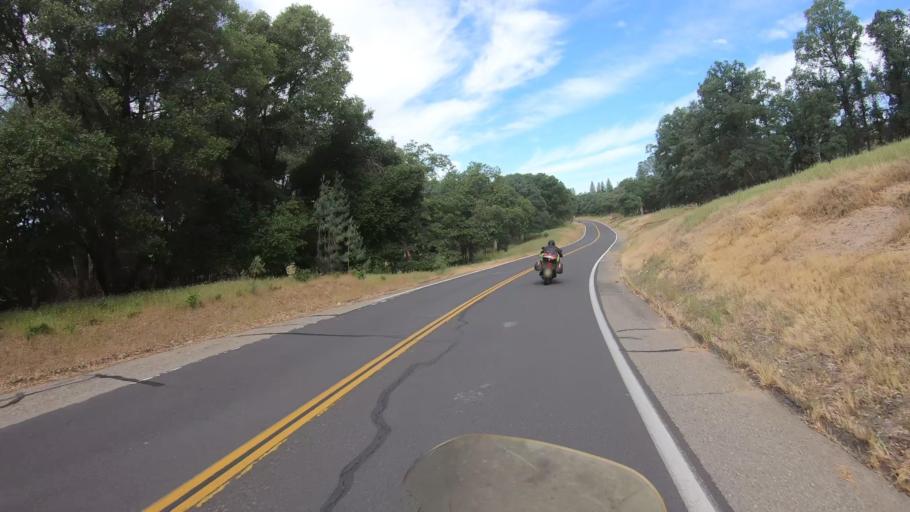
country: US
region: California
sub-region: Tuolumne County
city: Tuolumne City
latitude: 37.8574
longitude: -120.1745
